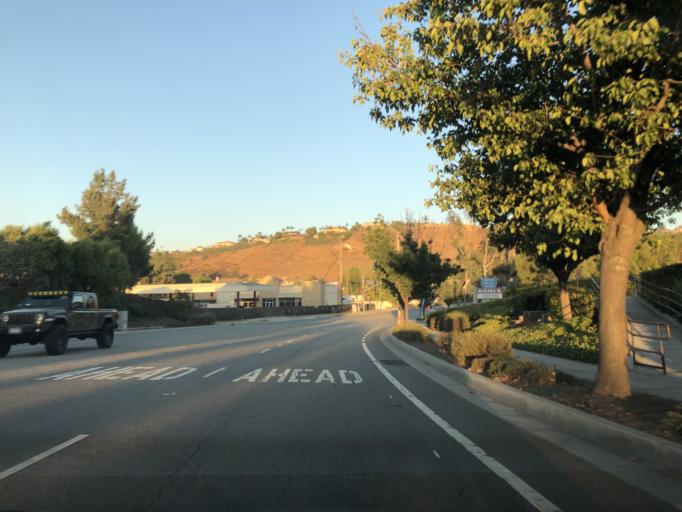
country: US
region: California
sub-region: Riverside County
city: Corona
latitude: 33.8996
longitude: -117.5551
